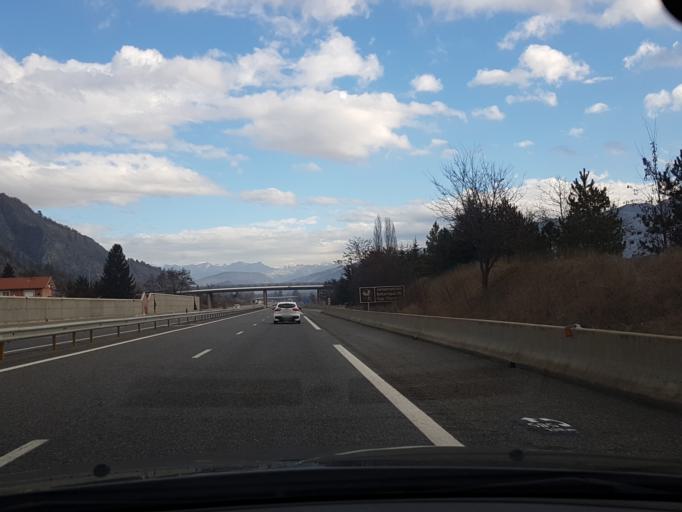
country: FR
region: Provence-Alpes-Cote d'Azur
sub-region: Departement des Hautes-Alpes
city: Tallard
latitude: 44.4241
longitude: 6.0099
